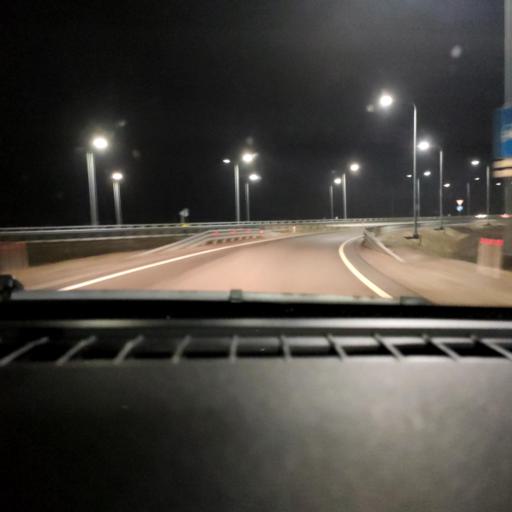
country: RU
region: Voronezj
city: Somovo
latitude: 51.7437
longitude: 39.3077
